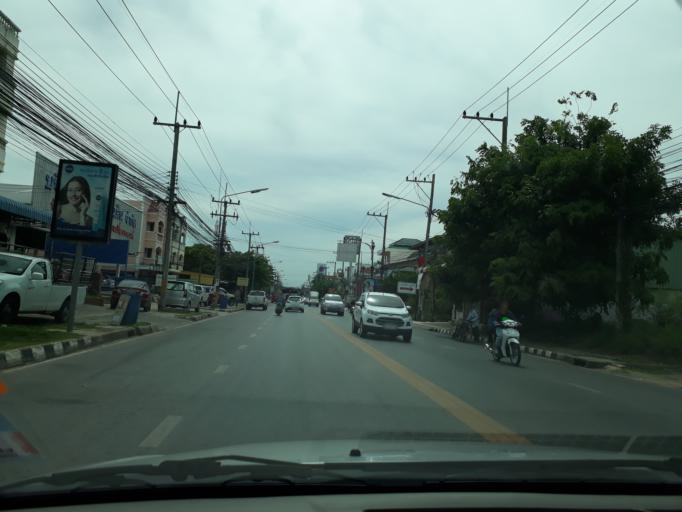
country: TH
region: Khon Kaen
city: Khon Kaen
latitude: 16.4355
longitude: 102.8536
